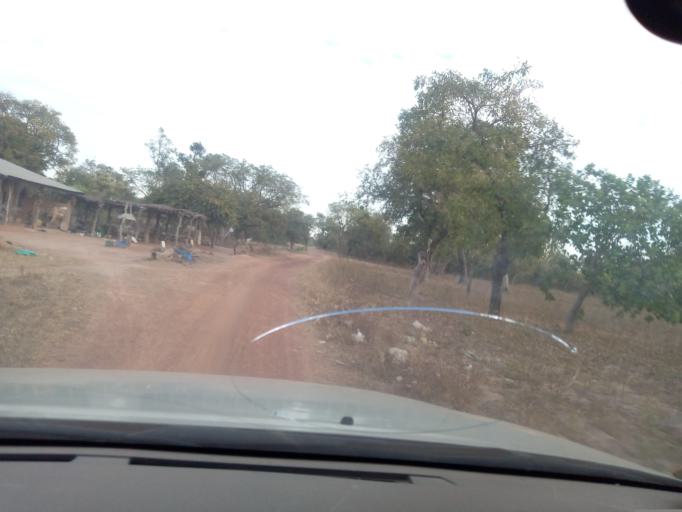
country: ML
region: Sikasso
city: Kadiolo
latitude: 10.5977
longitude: -5.8841
